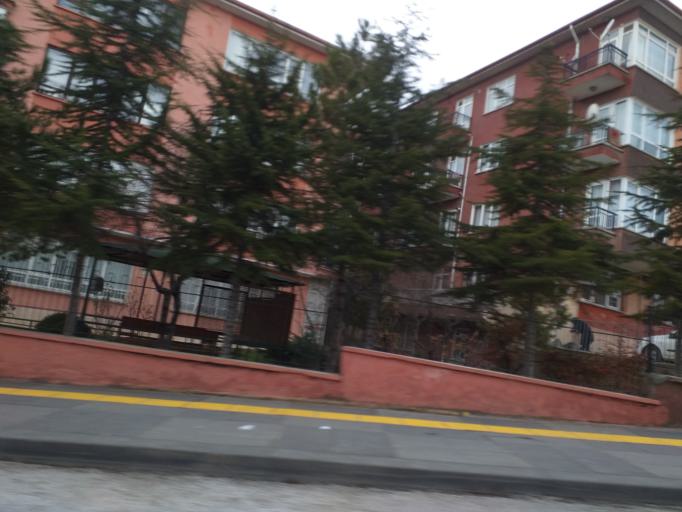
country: TR
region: Ankara
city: Ankara
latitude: 39.9762
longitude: 32.8294
